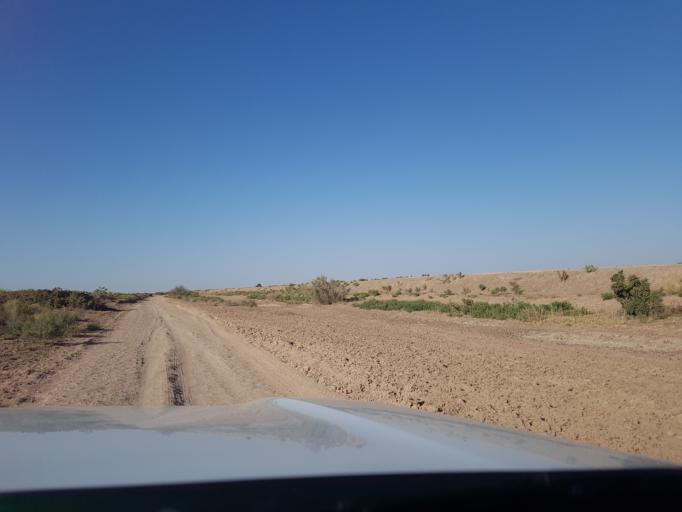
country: IR
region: Razavi Khorasan
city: Sarakhs
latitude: 36.9772
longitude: 61.3851
